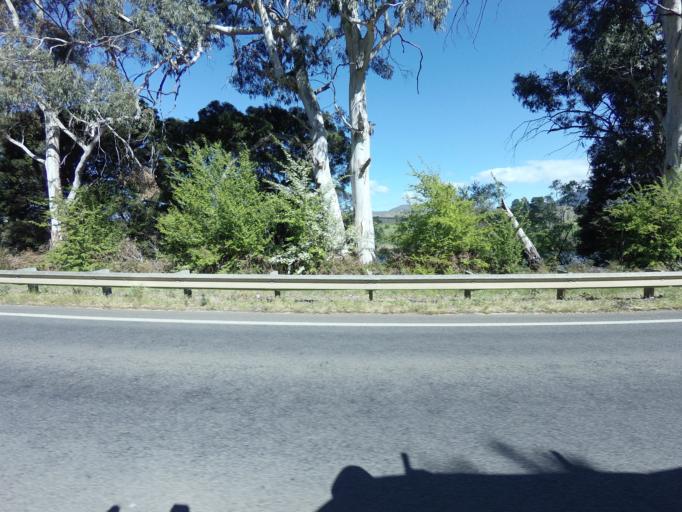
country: AU
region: Tasmania
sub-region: Derwent Valley
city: New Norfolk
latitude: -42.7352
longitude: 146.9612
